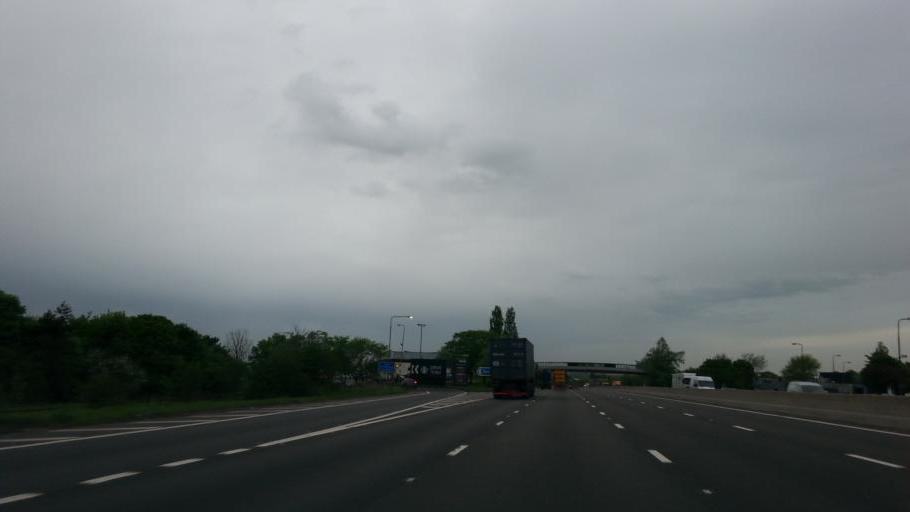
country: GB
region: England
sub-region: Rotherham
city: Harthill
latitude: 53.3131
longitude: -1.2832
